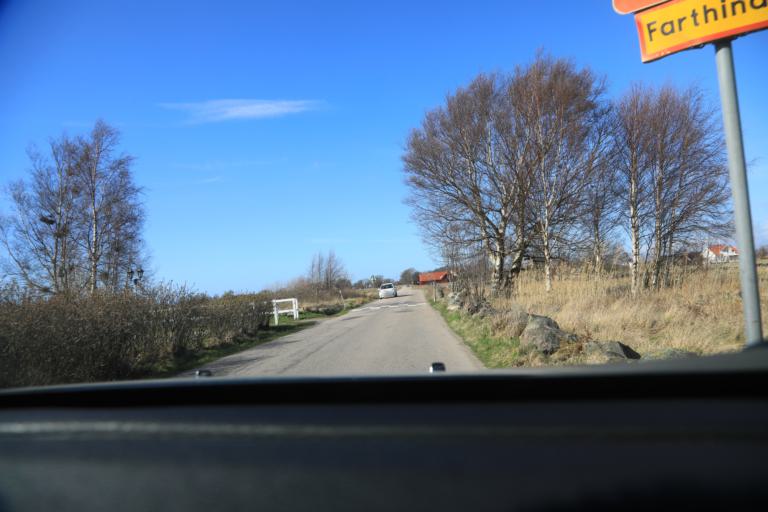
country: SE
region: Halland
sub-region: Varbergs Kommun
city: Varberg
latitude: 57.1173
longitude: 12.2234
